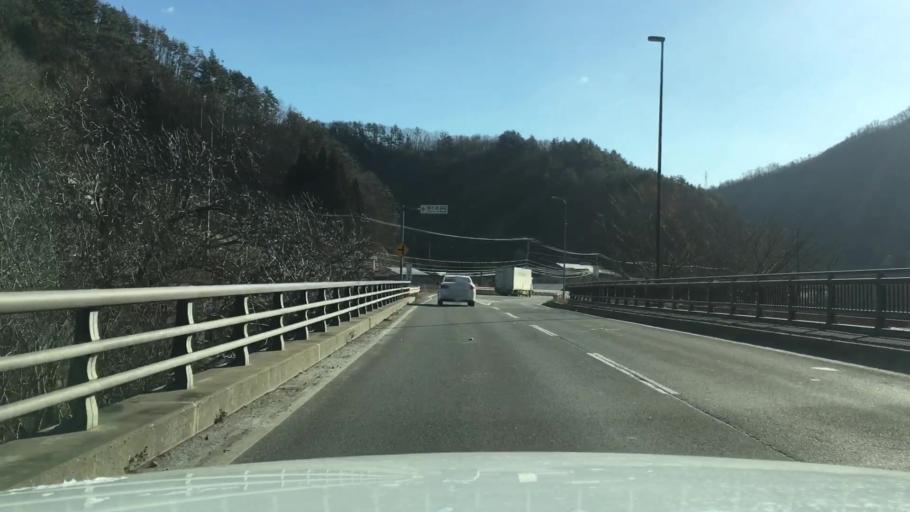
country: JP
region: Iwate
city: Tono
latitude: 39.6153
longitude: 141.6263
